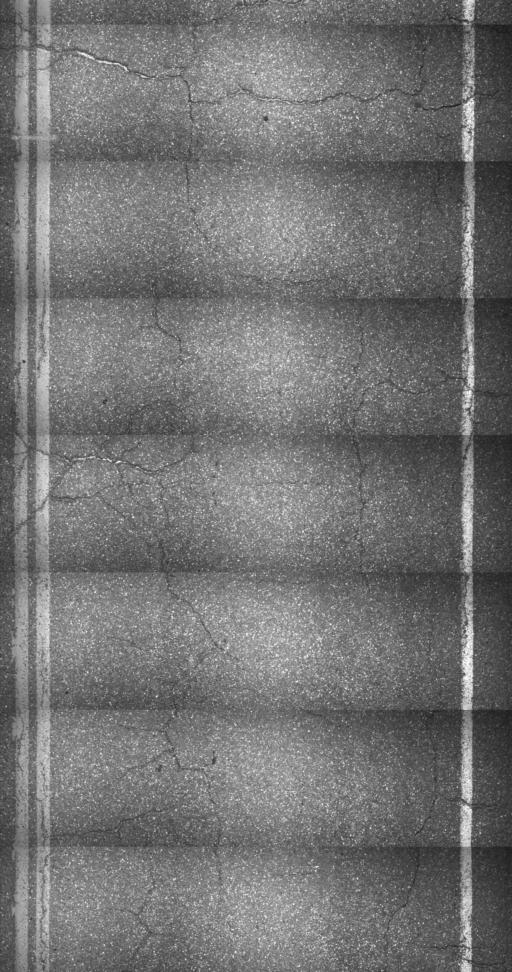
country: US
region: Vermont
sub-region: Lamoille County
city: Hyde Park
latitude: 44.5977
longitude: -72.6223
